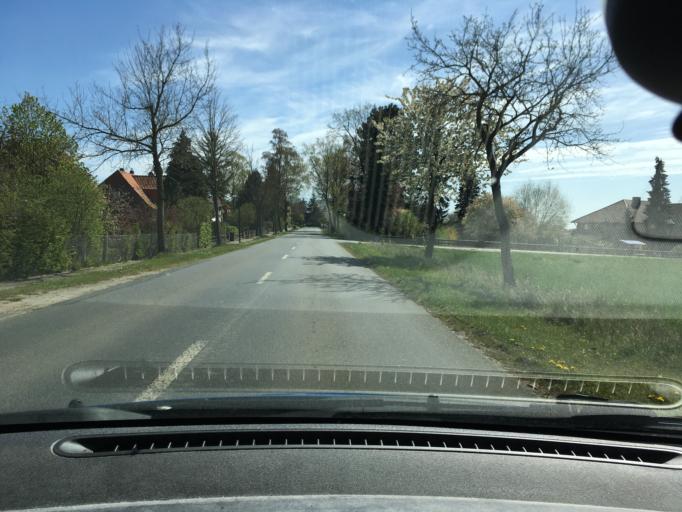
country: DE
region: Lower Saxony
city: Himbergen
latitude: 53.1303
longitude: 10.6942
